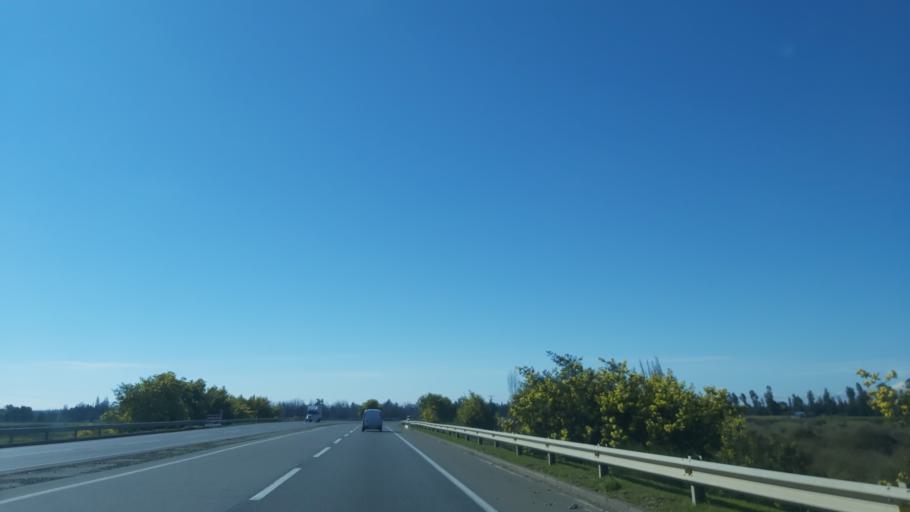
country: CL
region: Biobio
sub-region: Provincia de Nuble
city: Bulnes
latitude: -36.6547
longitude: -72.2407
